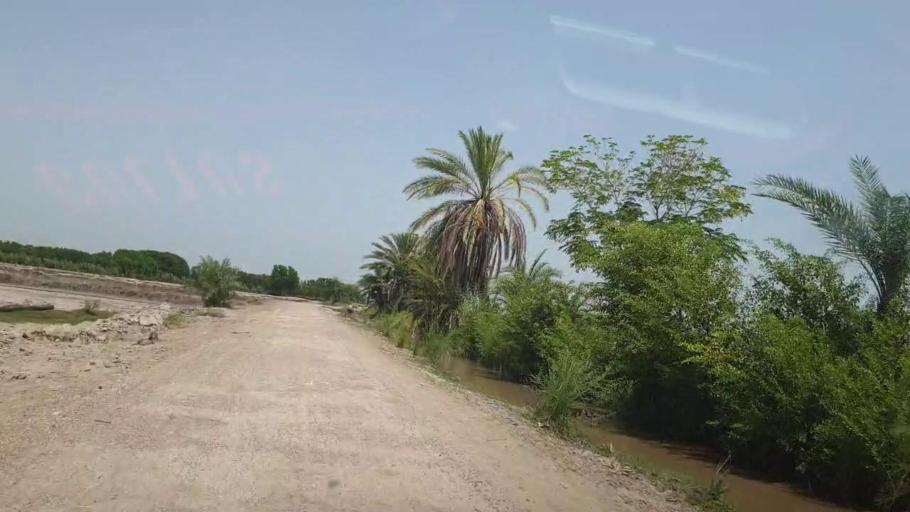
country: PK
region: Sindh
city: Daulatpur
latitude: 26.4882
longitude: 68.1397
